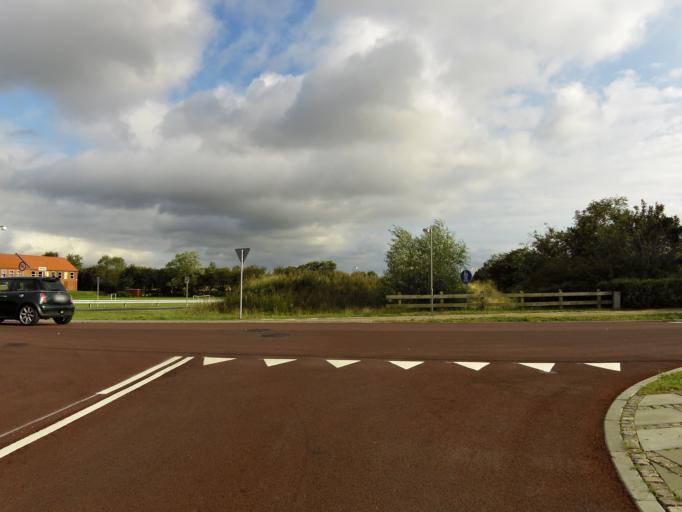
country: DK
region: South Denmark
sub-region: Esbjerg Kommune
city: Ribe
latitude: 55.3303
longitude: 8.7782
